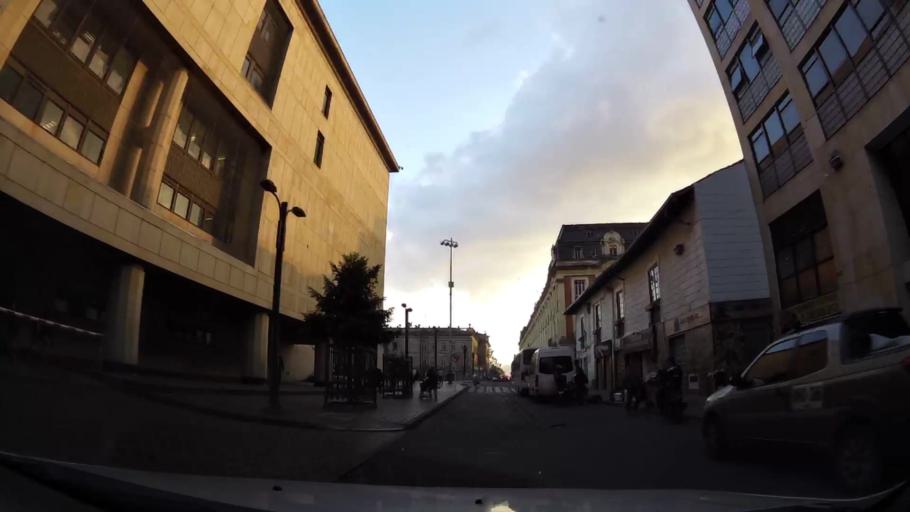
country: CO
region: Bogota D.C.
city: Bogota
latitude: 4.5992
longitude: -74.0760
